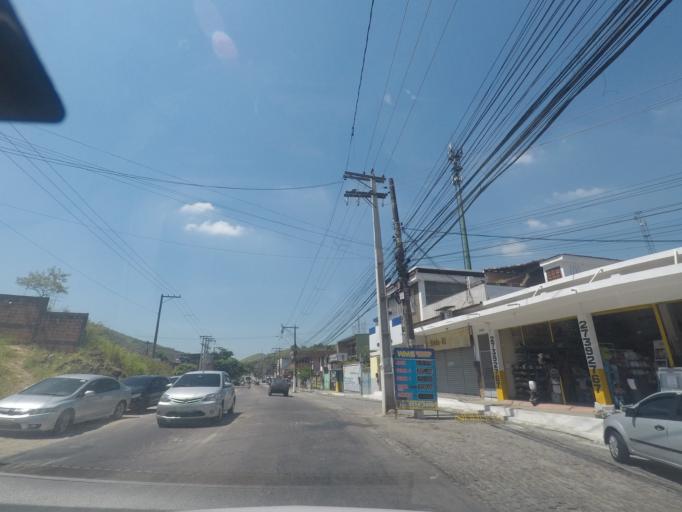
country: BR
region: Rio de Janeiro
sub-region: Petropolis
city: Petropolis
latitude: -22.5953
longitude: -43.1873
